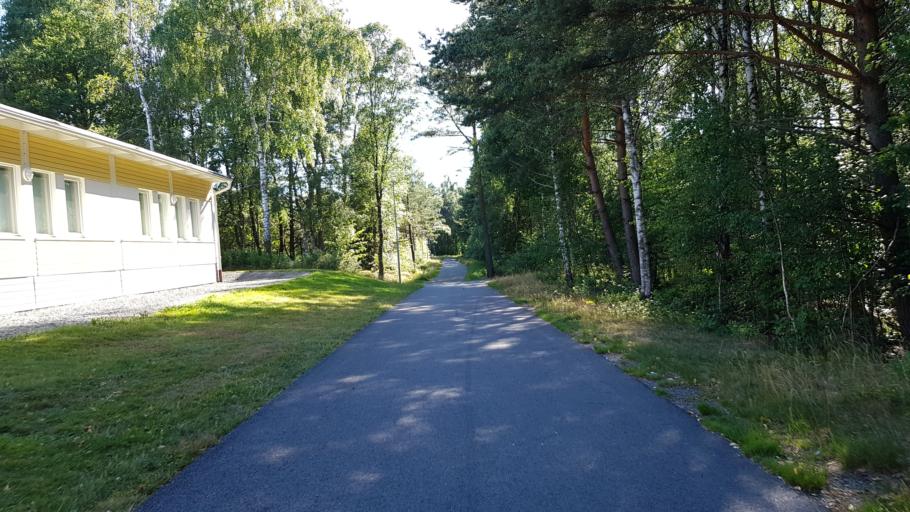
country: SE
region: Vaestra Goetaland
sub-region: Harryda Kommun
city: Molnlycke
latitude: 57.6519
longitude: 12.1239
